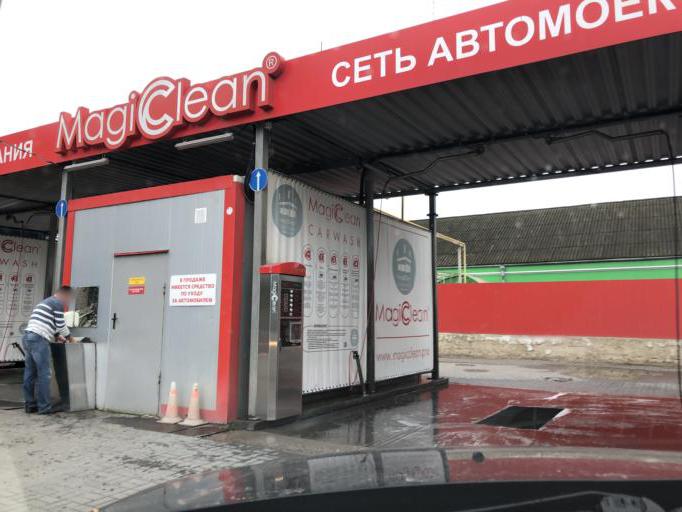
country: RU
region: Tula
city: Mendeleyevskiy
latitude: 54.1861
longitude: 37.5436
